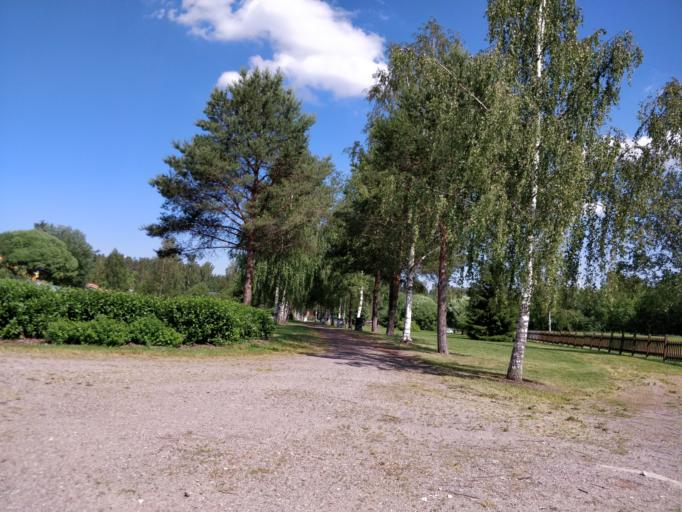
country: FI
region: Haeme
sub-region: Haemeenlinna
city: Tervakoski
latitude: 60.8086
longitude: 24.6150
